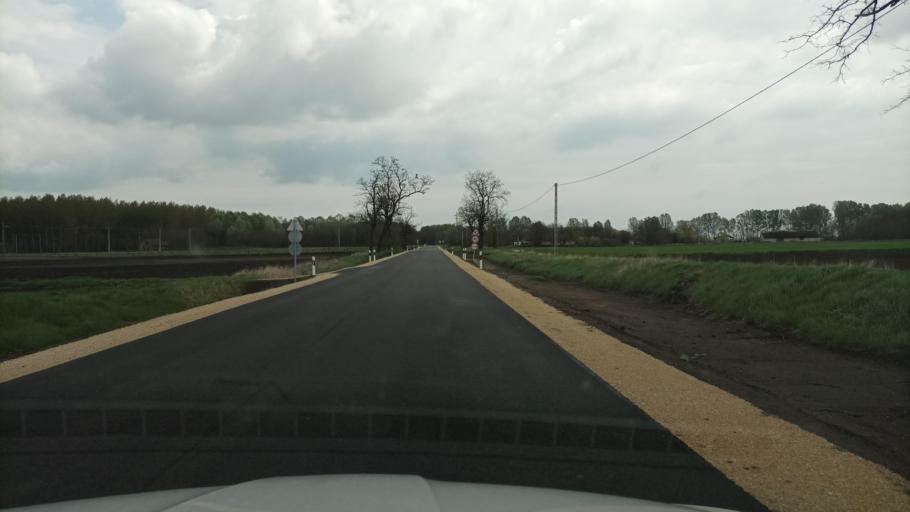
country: HU
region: Pest
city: Nagykoros
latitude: 47.0213
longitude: 19.8437
